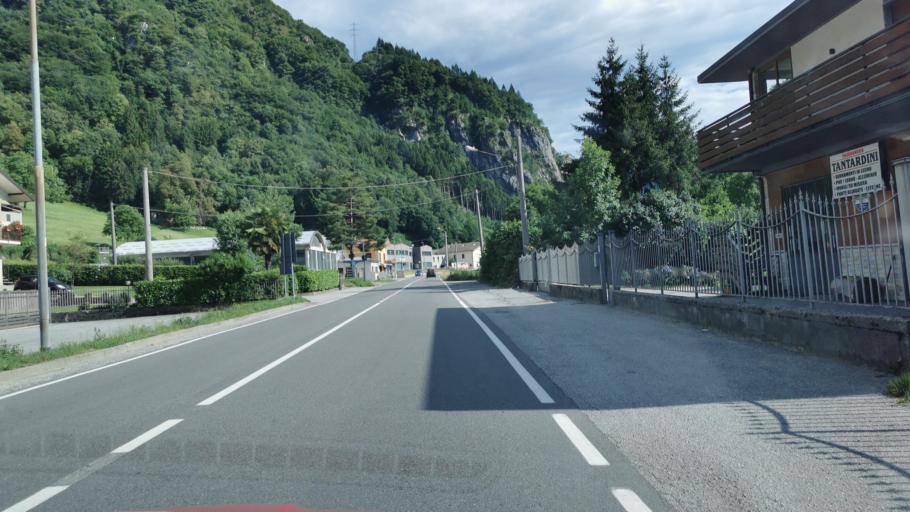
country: IT
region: Lombardy
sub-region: Provincia di Lecco
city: Introbio
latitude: 45.9655
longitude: 9.4504
